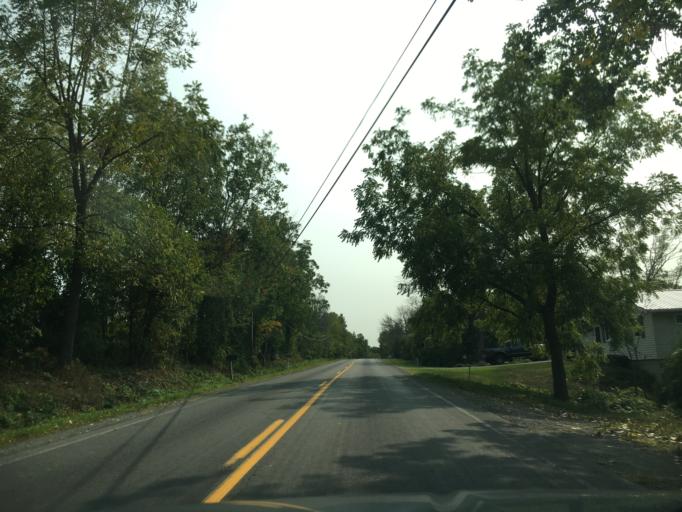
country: US
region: New York
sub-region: Steuben County
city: Sylvan Beach
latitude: 42.4636
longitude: -77.0979
